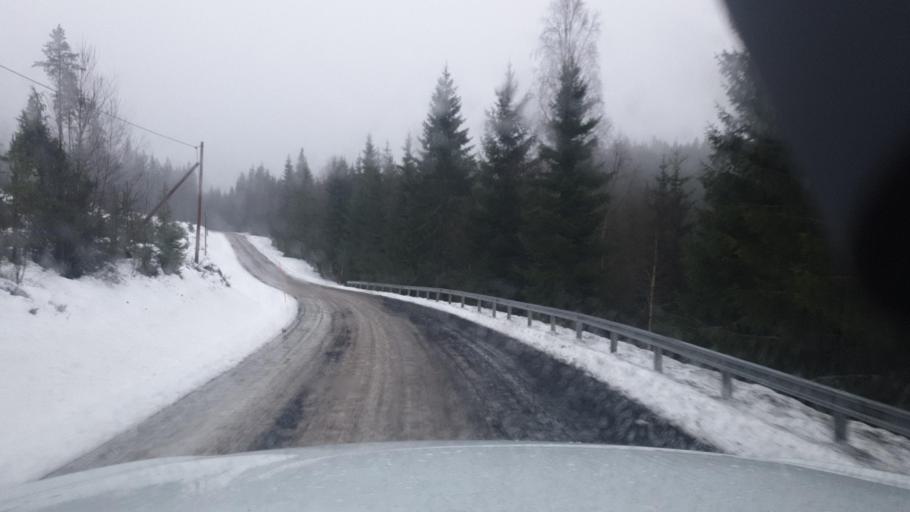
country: SE
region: Vaermland
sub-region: Eda Kommun
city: Charlottenberg
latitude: 60.1330
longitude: 12.5919
